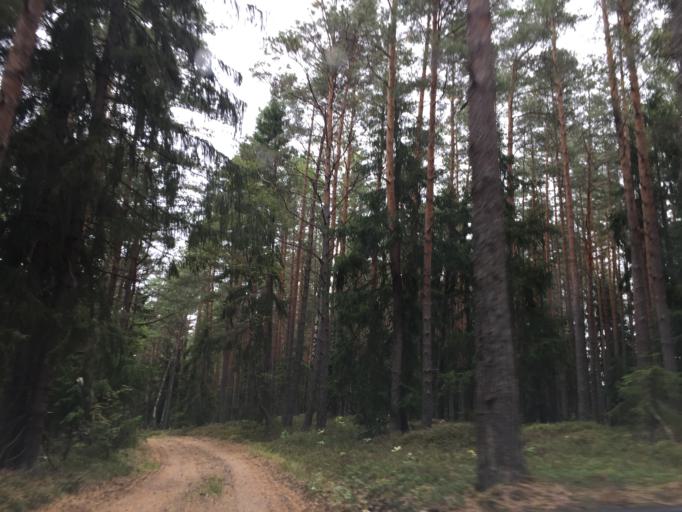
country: LV
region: Salacgrivas
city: Salacgriva
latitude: 57.7061
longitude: 24.3544
